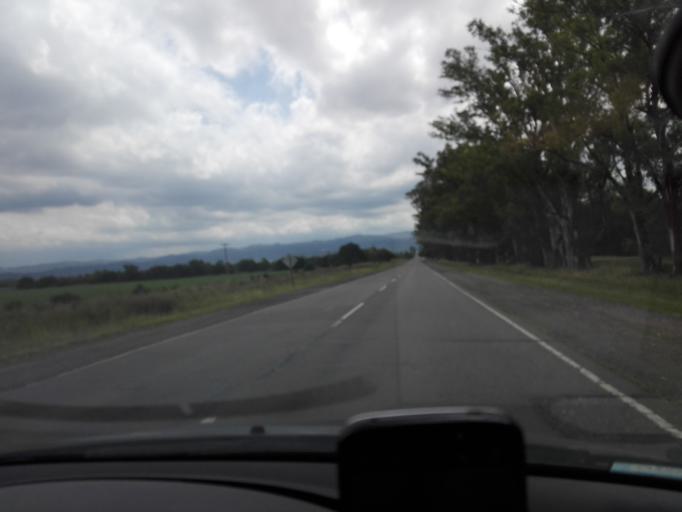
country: AR
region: Cordoba
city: Alta Gracia
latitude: -31.6582
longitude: -64.3855
